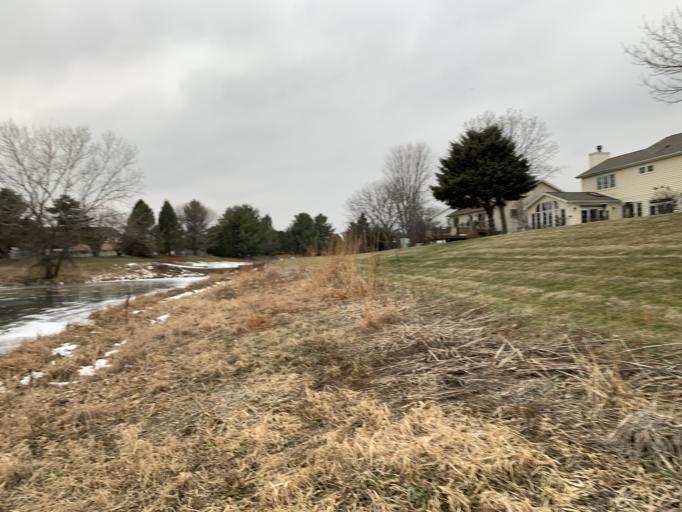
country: US
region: Wisconsin
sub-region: Dane County
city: Middleton
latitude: 43.0794
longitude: -89.5165
